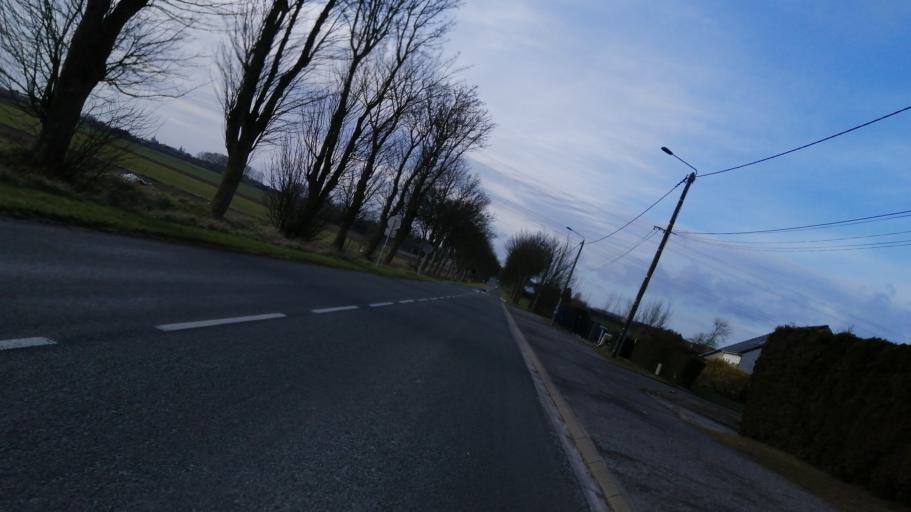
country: FR
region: Nord-Pas-de-Calais
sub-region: Departement du Pas-de-Calais
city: Beaurains
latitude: 50.2513
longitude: 2.8096
